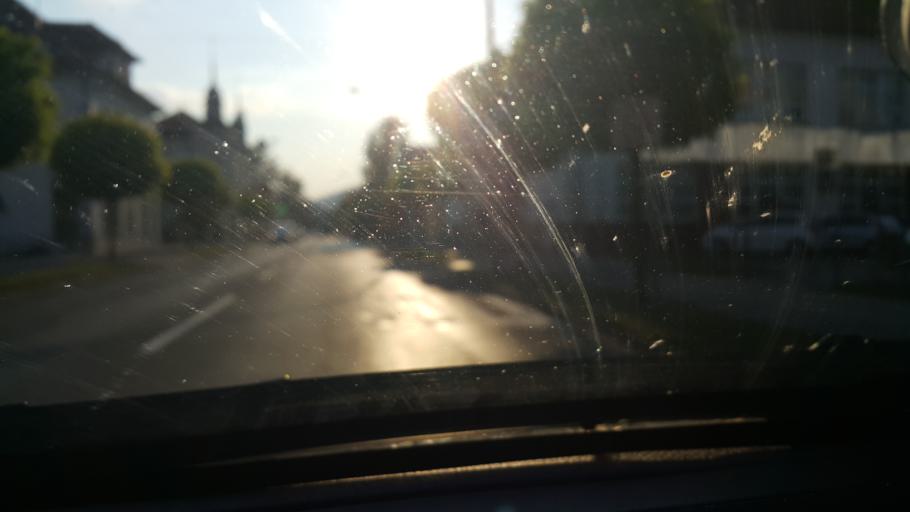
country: SI
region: Domzale
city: Domzale
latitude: 46.1379
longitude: 14.5933
